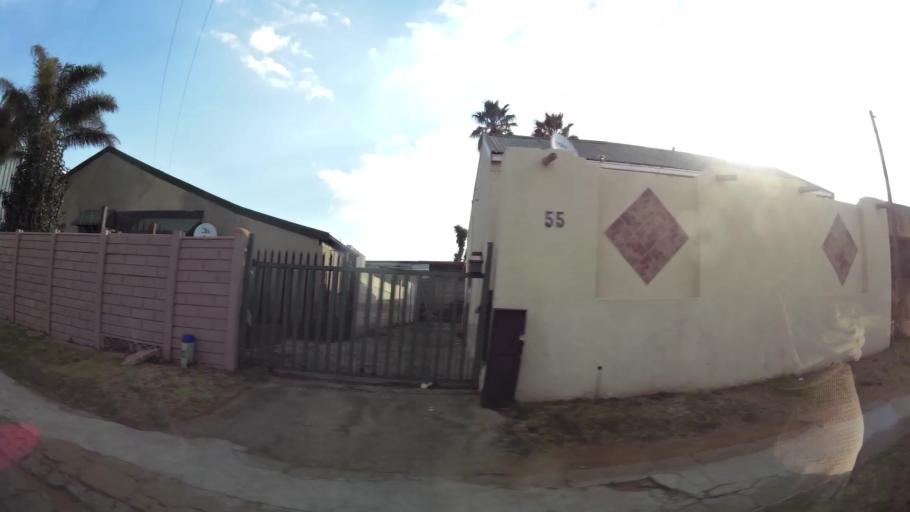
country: ZA
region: Gauteng
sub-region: West Rand District Municipality
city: Krugersdorp
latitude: -26.0971
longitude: 27.7529
